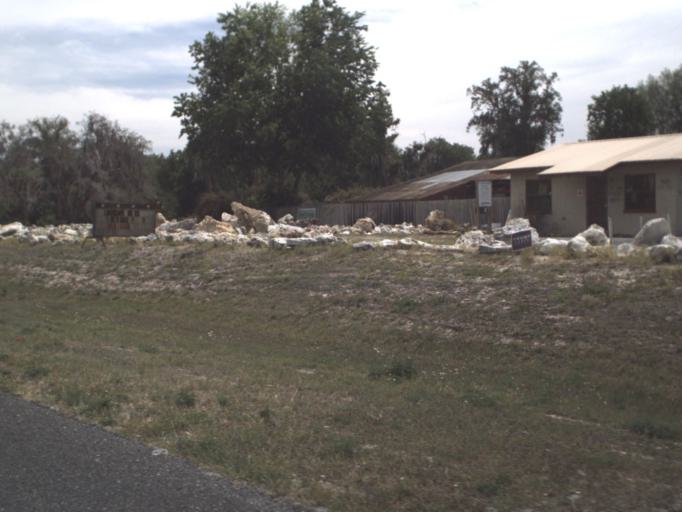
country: US
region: Florida
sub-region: Sumter County
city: Wildwood
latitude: 28.8268
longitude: -81.9922
